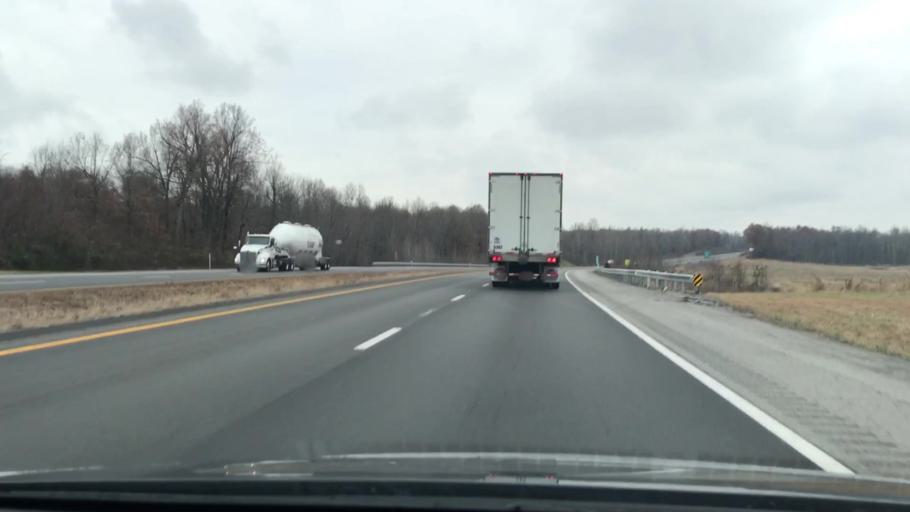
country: US
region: Kentucky
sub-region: Hopkins County
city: Madisonville
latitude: 37.4611
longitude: -87.4805
